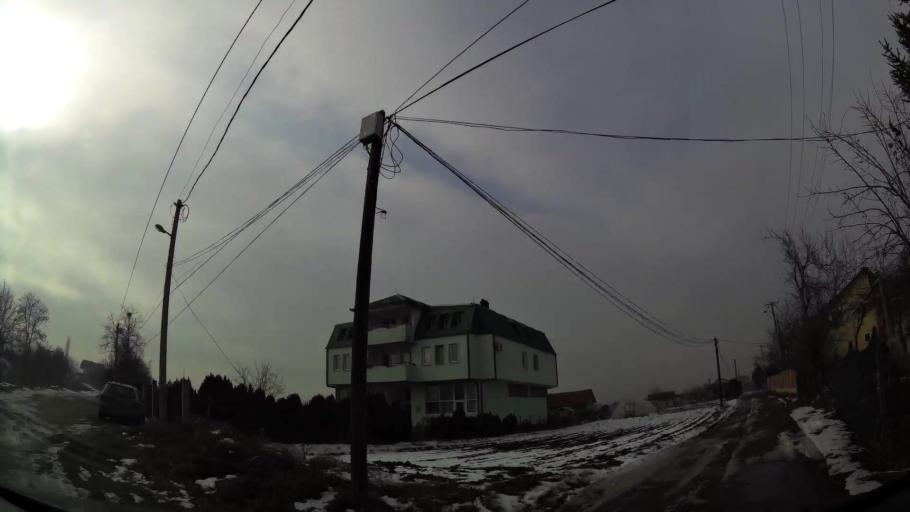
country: MK
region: Ilinden
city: Ilinden
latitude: 41.9882
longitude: 21.5829
